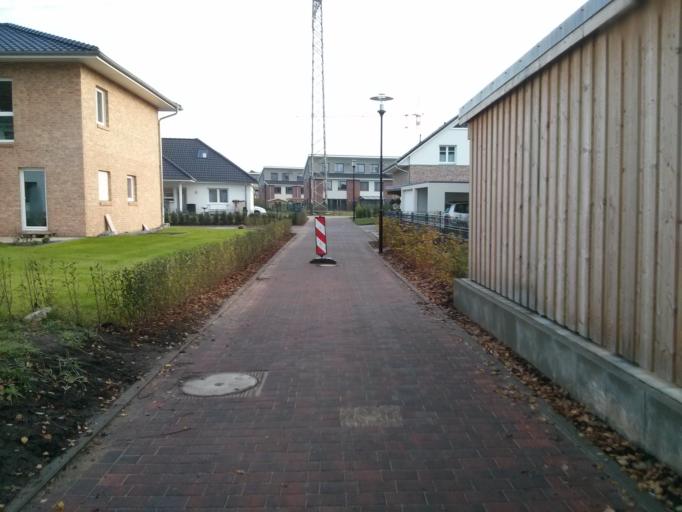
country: DE
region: Schleswig-Holstein
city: Ellerbek
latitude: 53.6338
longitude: 9.8686
